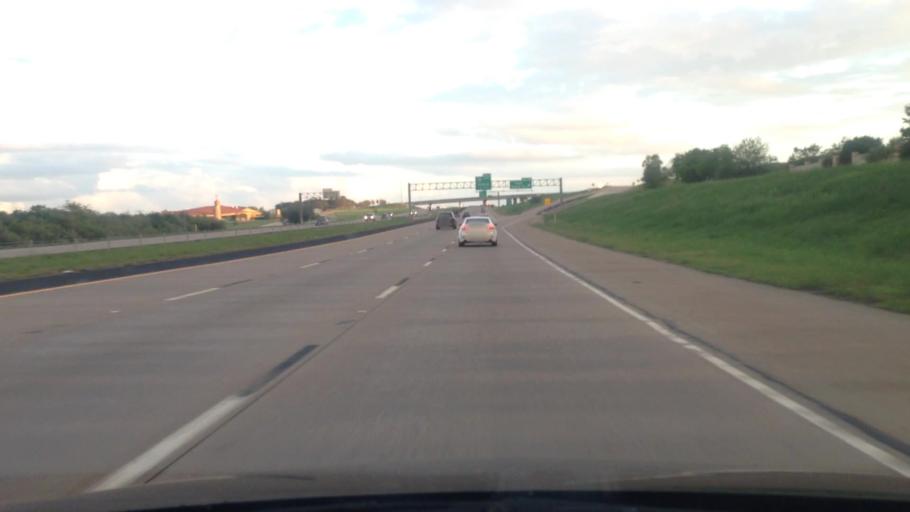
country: US
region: Texas
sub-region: Tarrant County
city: Benbrook
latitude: 32.7088
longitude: -97.4760
